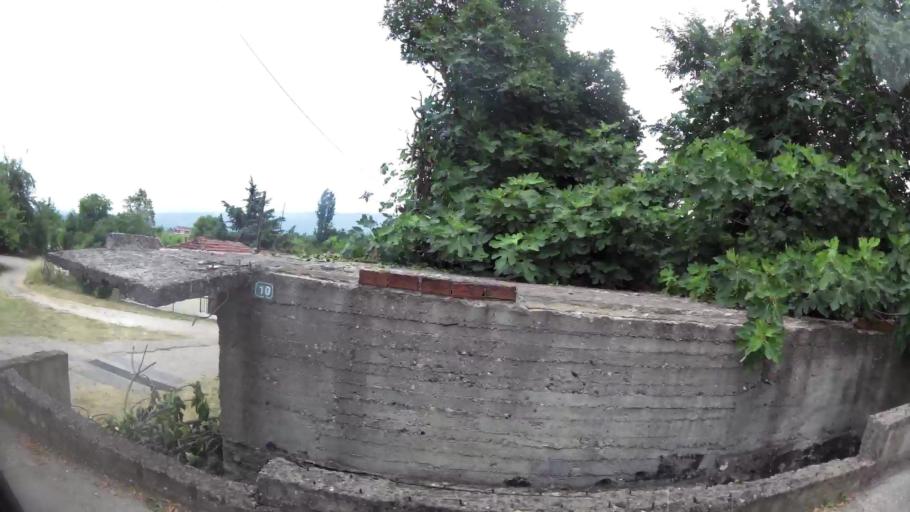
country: GR
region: Central Macedonia
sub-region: Nomos Imathias
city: Veroia
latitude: 40.5200
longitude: 22.2096
